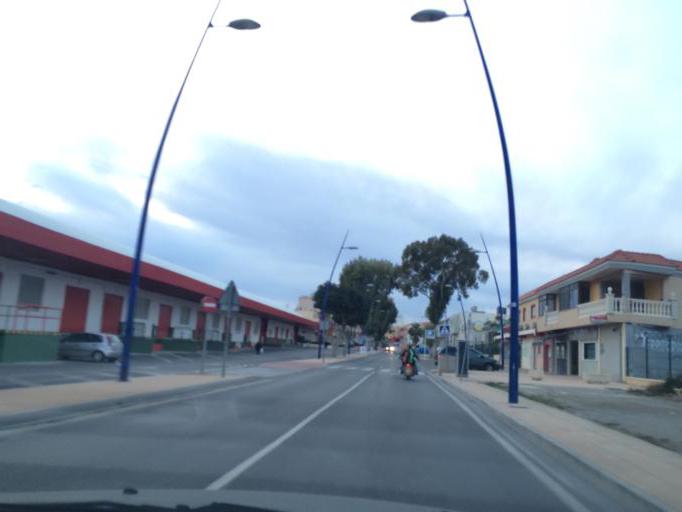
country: ES
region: Andalusia
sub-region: Provincia de Almeria
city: Viator
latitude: 36.8405
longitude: -2.4015
